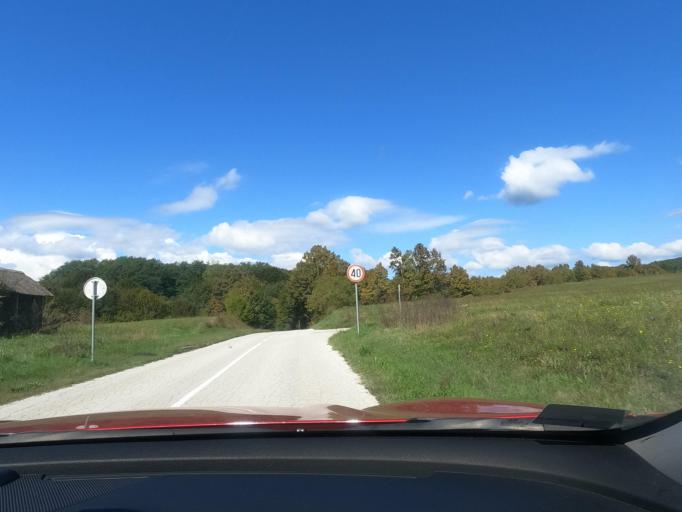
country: BA
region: Federation of Bosnia and Herzegovina
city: Podzvizd
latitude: 45.2293
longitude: 15.8963
